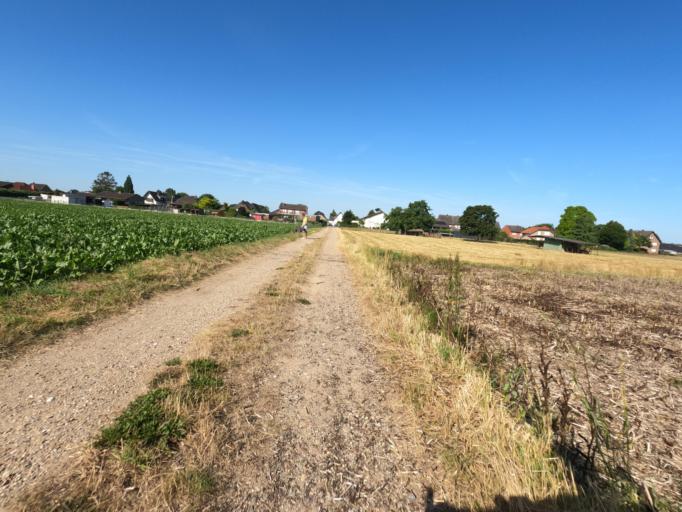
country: DE
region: North Rhine-Westphalia
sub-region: Regierungsbezirk Koln
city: Heinsberg
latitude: 51.0749
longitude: 6.1186
